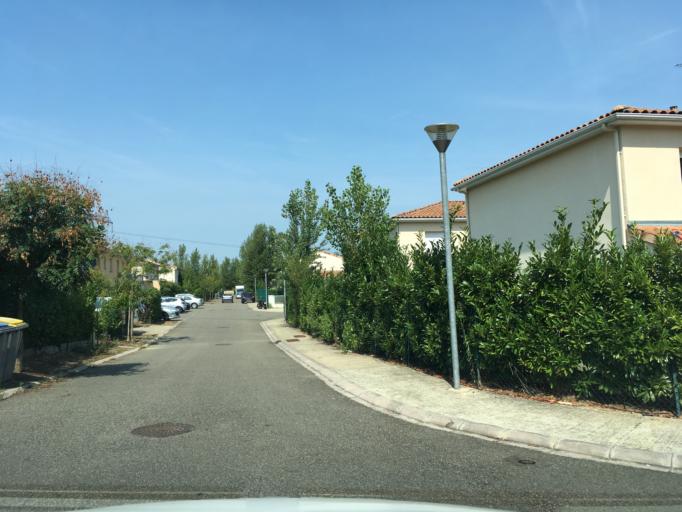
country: FR
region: Midi-Pyrenees
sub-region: Departement du Tarn-et-Garonne
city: Saint-Nauphary
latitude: 44.0074
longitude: 1.4022
